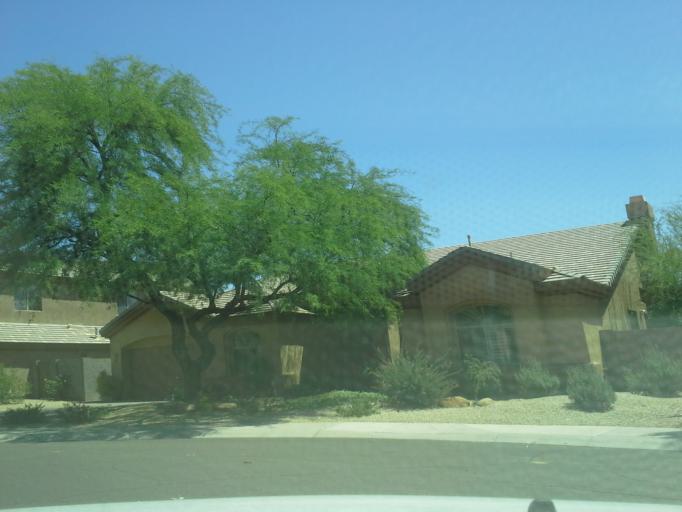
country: US
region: Arizona
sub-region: Maricopa County
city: Paradise Valley
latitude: 33.6172
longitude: -111.9383
